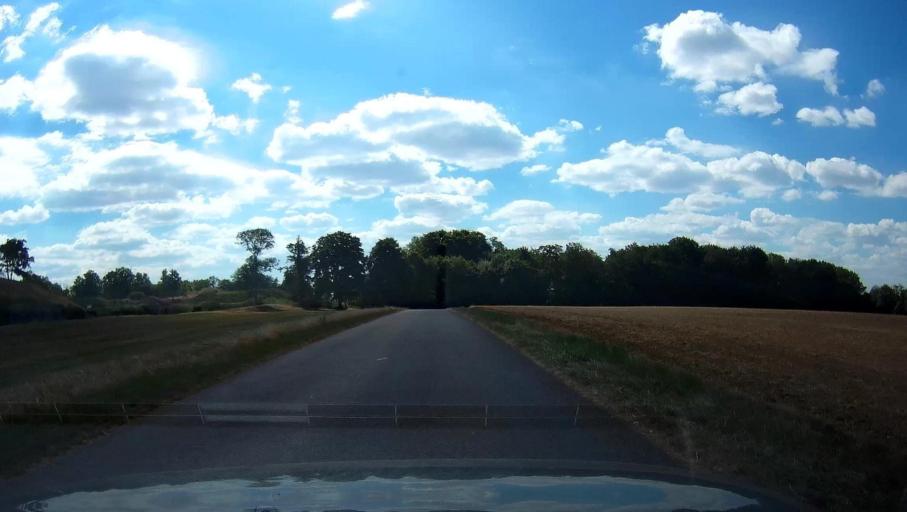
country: FR
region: Champagne-Ardenne
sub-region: Departement de la Haute-Marne
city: Langres
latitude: 47.8762
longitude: 5.3627
